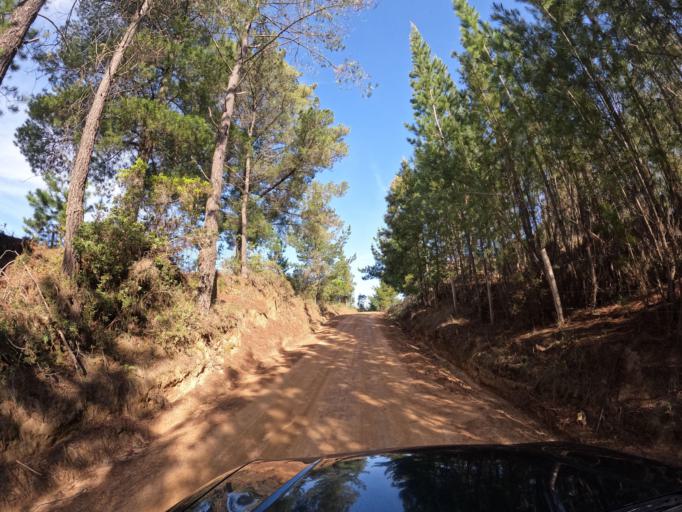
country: CL
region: Biobio
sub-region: Provincia de Biobio
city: La Laja
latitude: -37.1219
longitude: -72.7363
